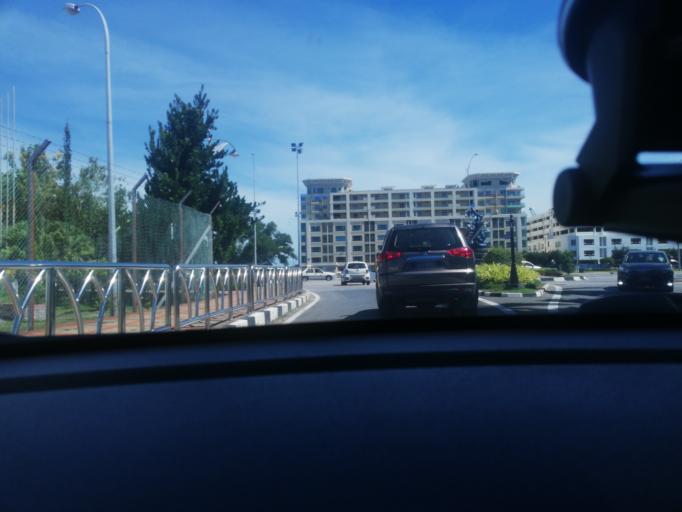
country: MY
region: Labuan
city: Victoria
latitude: 5.2766
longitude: 115.2461
